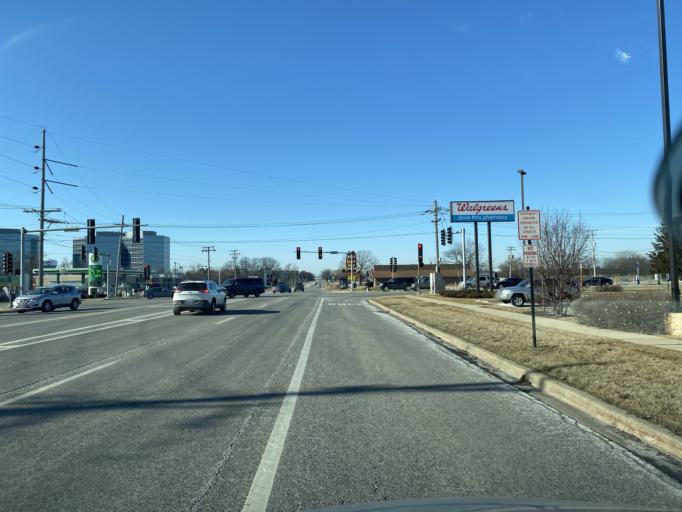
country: US
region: Illinois
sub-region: Cook County
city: Westchester
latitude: 41.8483
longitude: -87.9006
